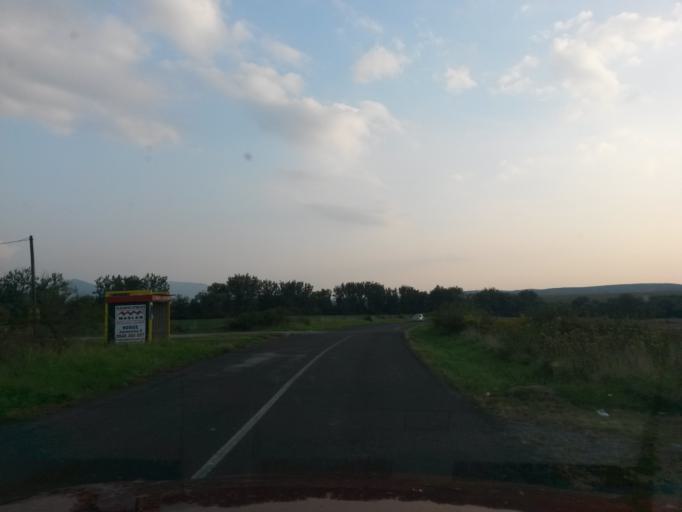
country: SK
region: Kosicky
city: Kosice
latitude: 48.7581
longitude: 21.4341
